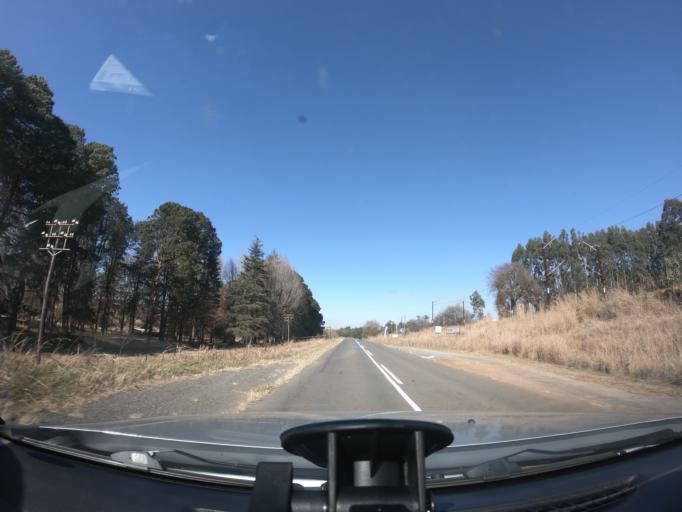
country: ZA
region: KwaZulu-Natal
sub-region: uMgungundlovu District Municipality
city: Howick
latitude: -29.4152
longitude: 30.0889
